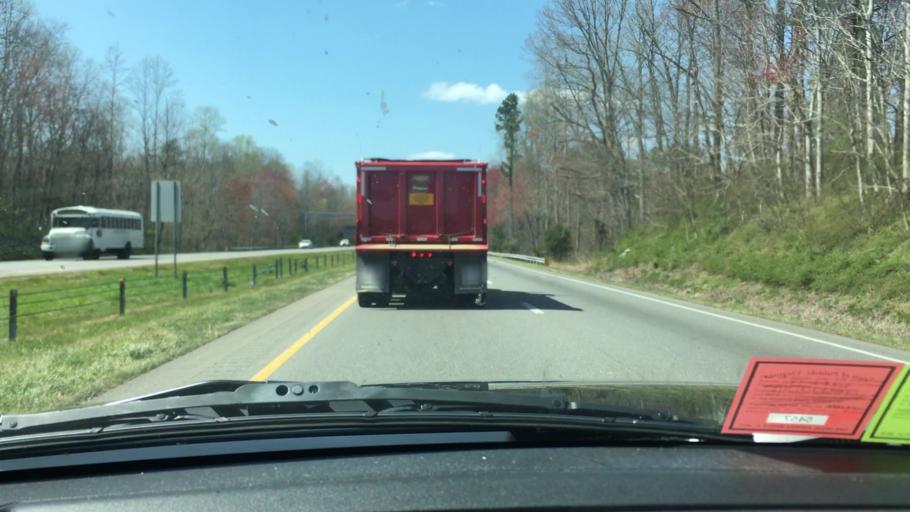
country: US
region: North Carolina
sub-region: Surry County
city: Pilot Mountain
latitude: 36.4338
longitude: -80.5299
